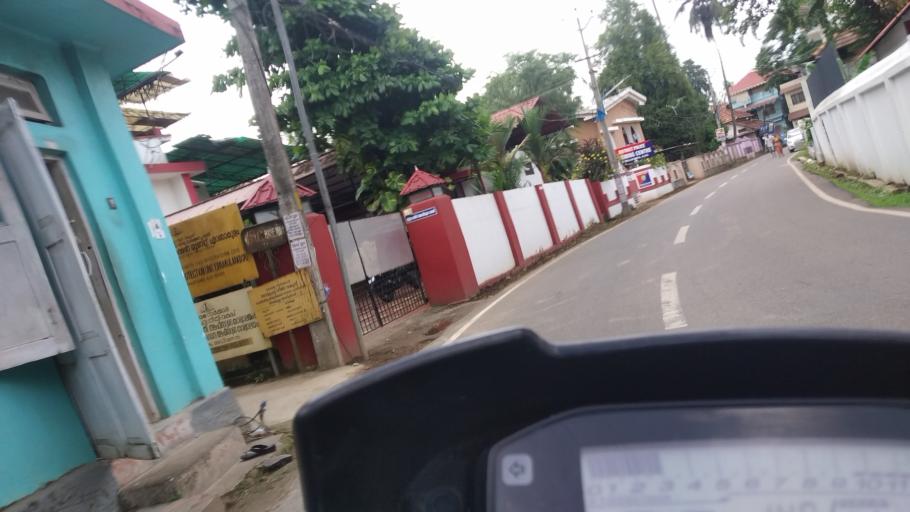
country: IN
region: Kerala
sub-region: Ernakulam
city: Aluva
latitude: 10.1157
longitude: 76.3497
